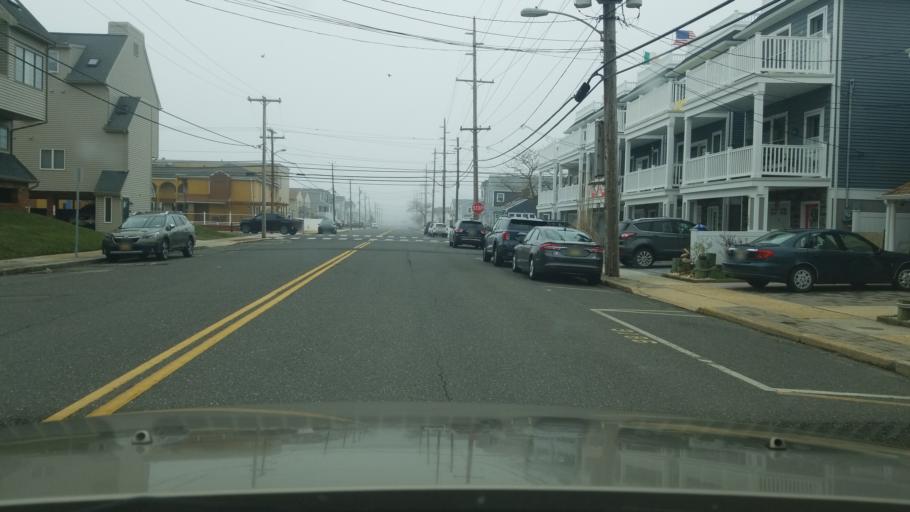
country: US
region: New Jersey
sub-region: Ocean County
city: Seaside Heights
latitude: 39.9483
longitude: -74.0735
